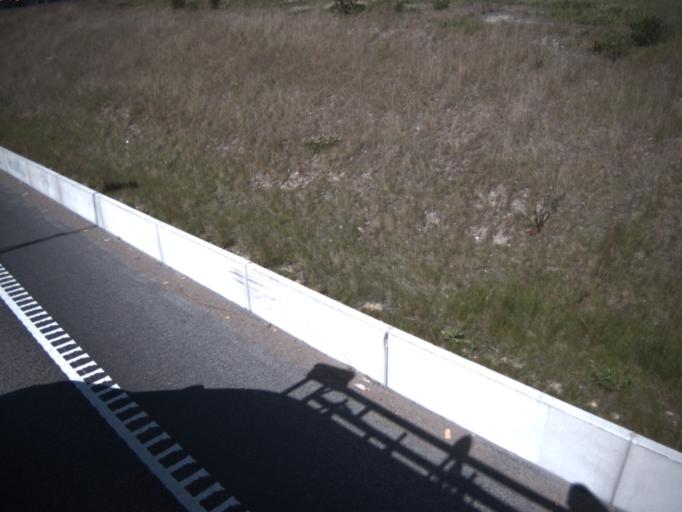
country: SE
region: Skane
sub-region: Helsingborg
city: Odakra
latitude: 56.0528
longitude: 12.7518
